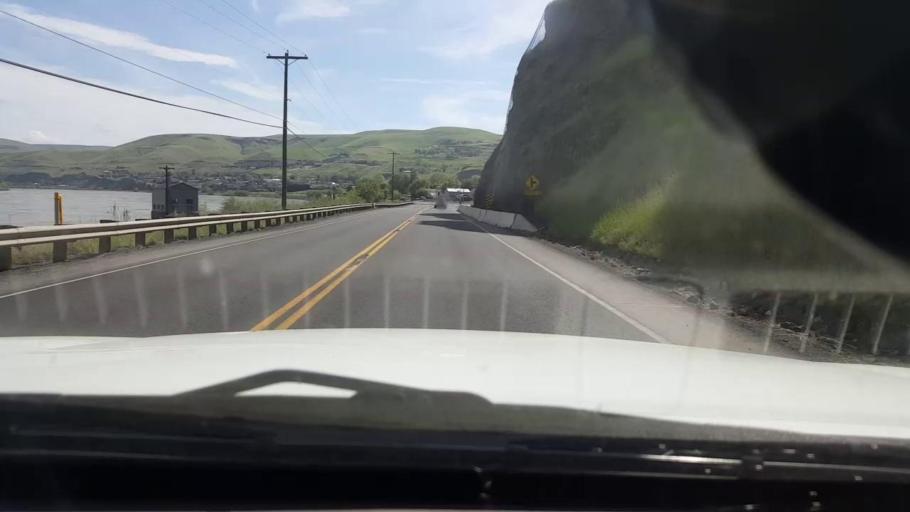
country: US
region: Washington
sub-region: Asotin County
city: Clarkston Heights-Vineland
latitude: 46.3702
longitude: -117.0616
